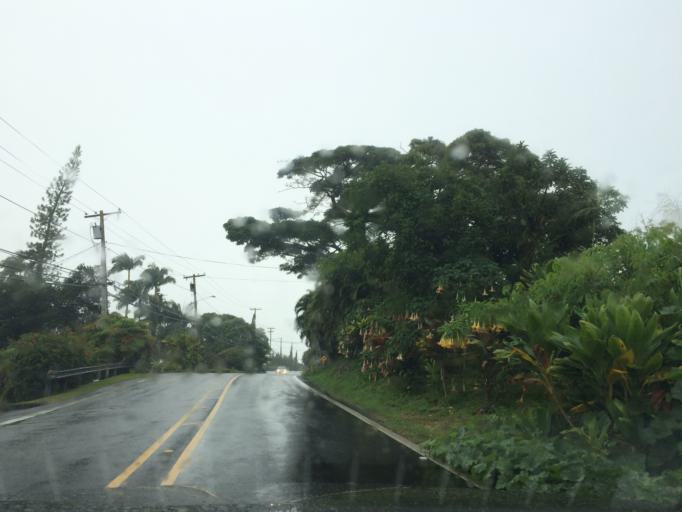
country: US
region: Hawaii
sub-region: Hawaii County
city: Hilo
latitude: 19.7015
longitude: -155.1140
